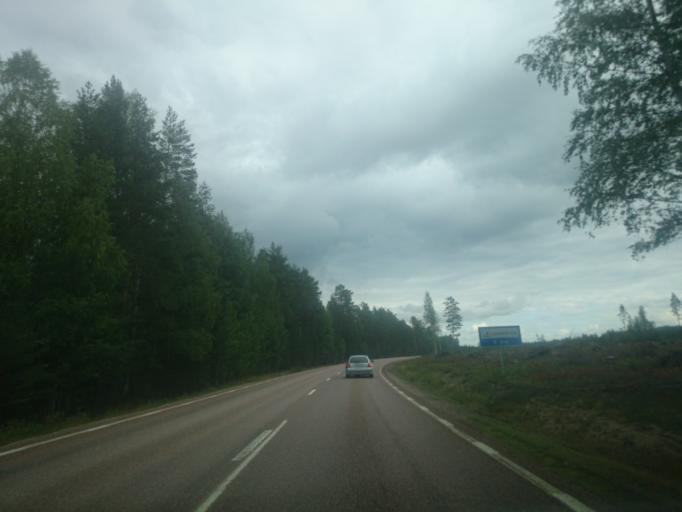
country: SE
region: Gaevleborg
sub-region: Ljusdals Kommun
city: Farila
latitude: 61.9434
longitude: 15.4625
